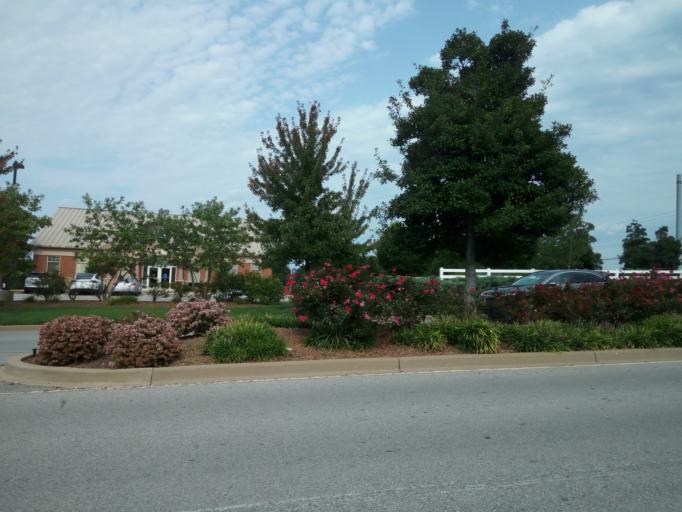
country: US
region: Kentucky
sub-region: Jefferson County
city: Worthington
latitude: 38.3114
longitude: -85.5707
